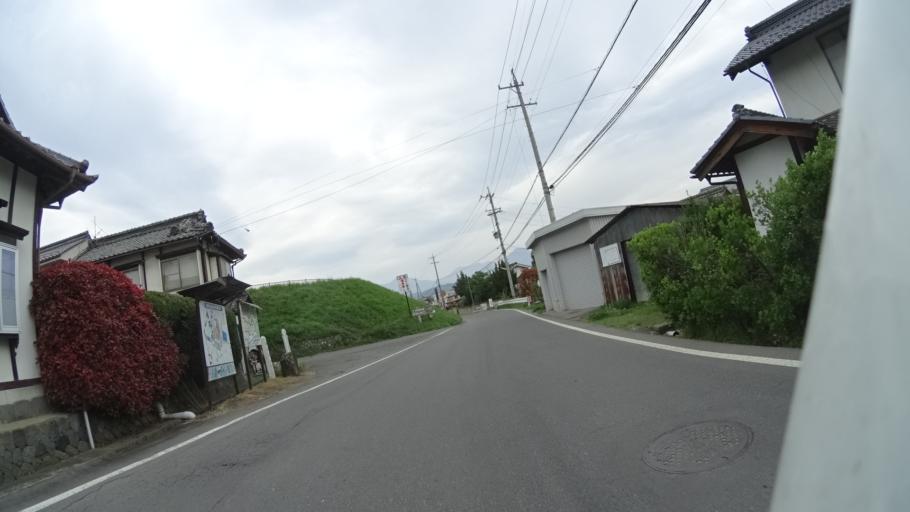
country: JP
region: Nagano
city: Kamimaruko
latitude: 36.3485
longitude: 138.2027
